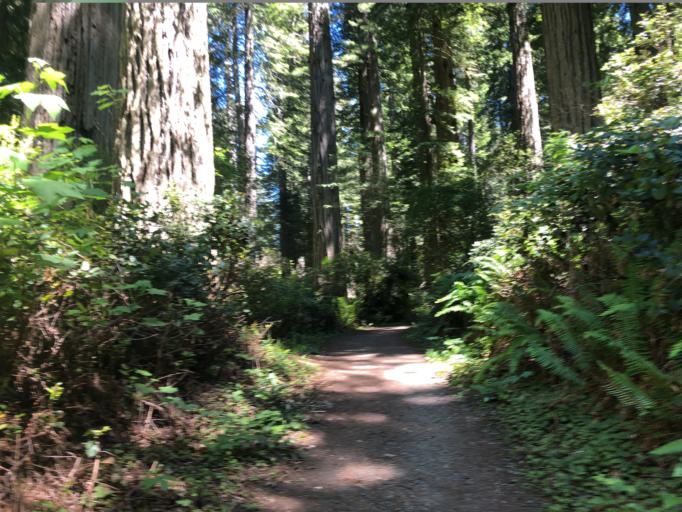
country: US
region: California
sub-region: Humboldt County
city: Westhaven-Moonstone
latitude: 41.3088
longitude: -124.0250
